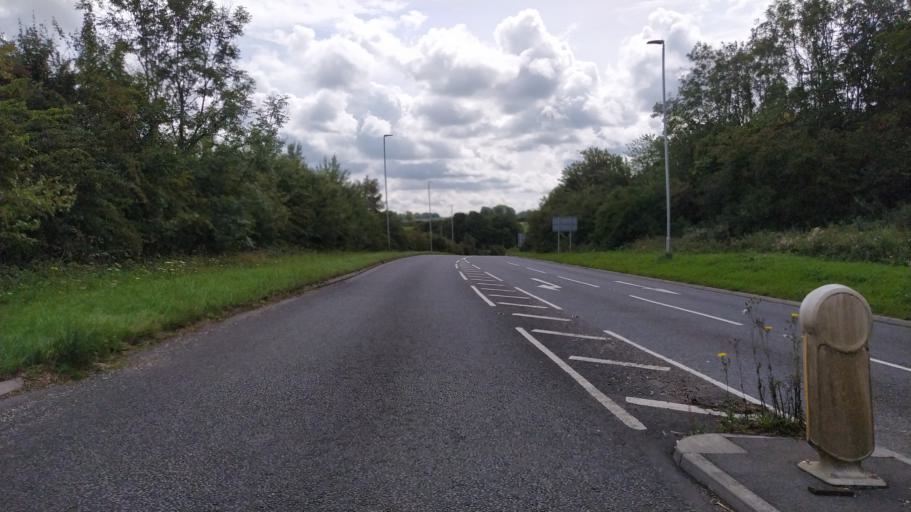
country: GB
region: England
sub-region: Wiltshire
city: Hindon
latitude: 51.0977
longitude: -2.1618
